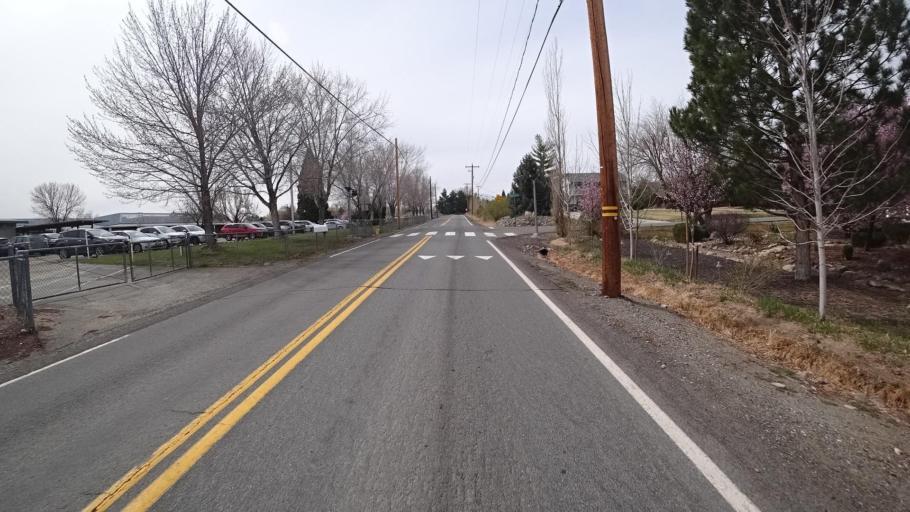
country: US
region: Nevada
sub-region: Washoe County
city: Reno
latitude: 39.4327
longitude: -119.7755
